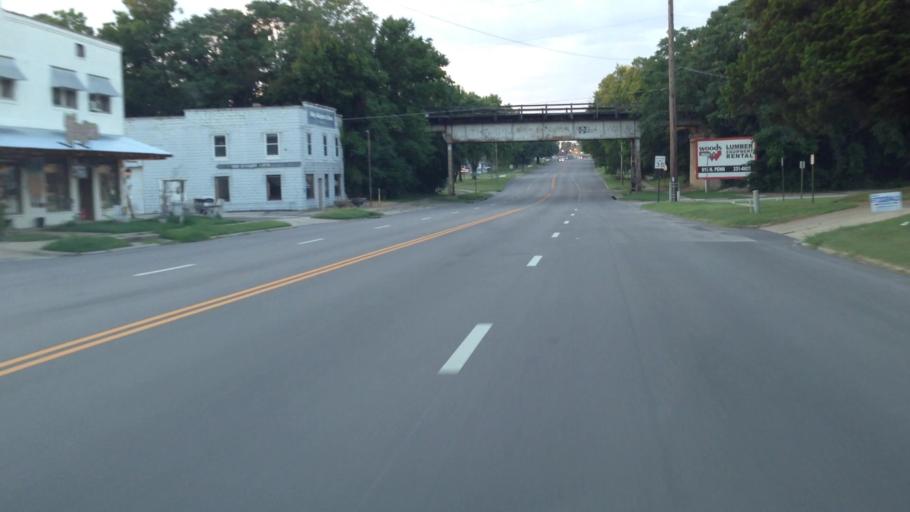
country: US
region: Kansas
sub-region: Montgomery County
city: Independence
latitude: 37.2315
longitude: -95.7065
